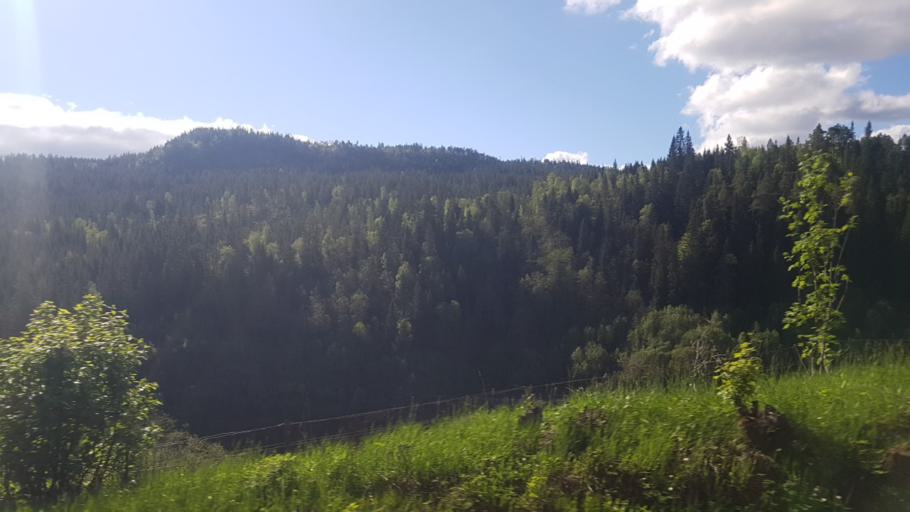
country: NO
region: Sor-Trondelag
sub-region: Midtre Gauldal
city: Storen
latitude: 62.9463
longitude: 10.1890
